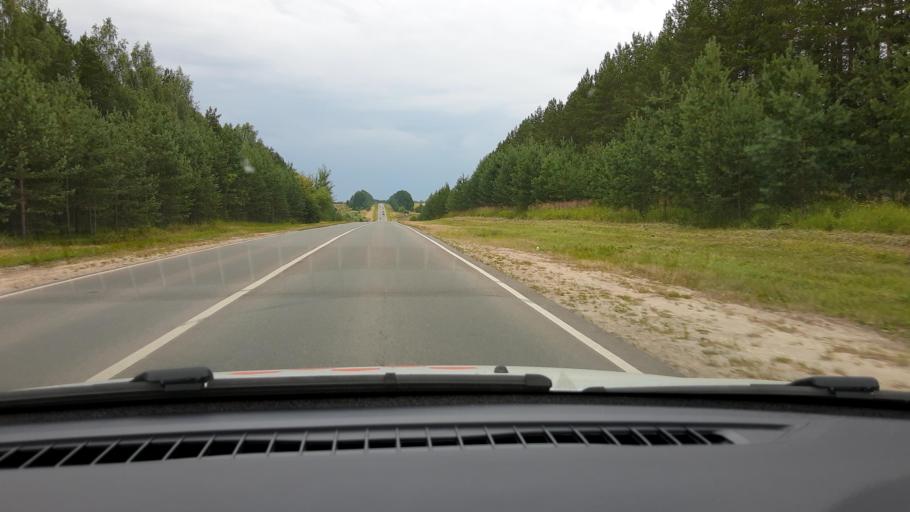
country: RU
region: Nizjnij Novgorod
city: Sarov
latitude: 55.1382
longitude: 43.5586
